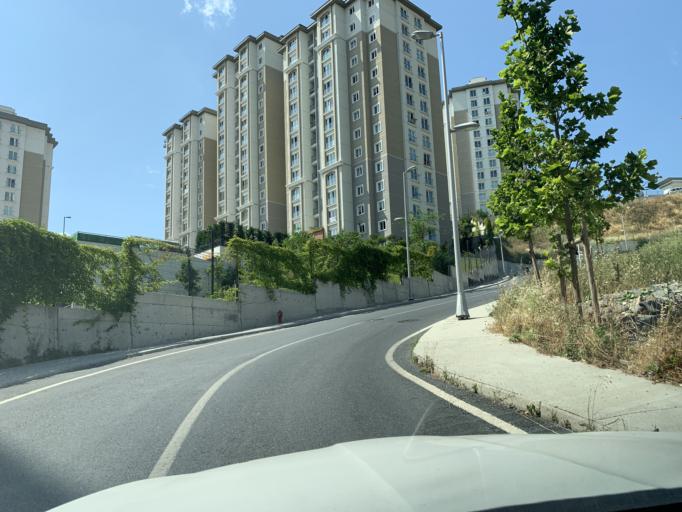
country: TR
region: Istanbul
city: Esenyurt
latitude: 41.0799
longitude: 28.6924
